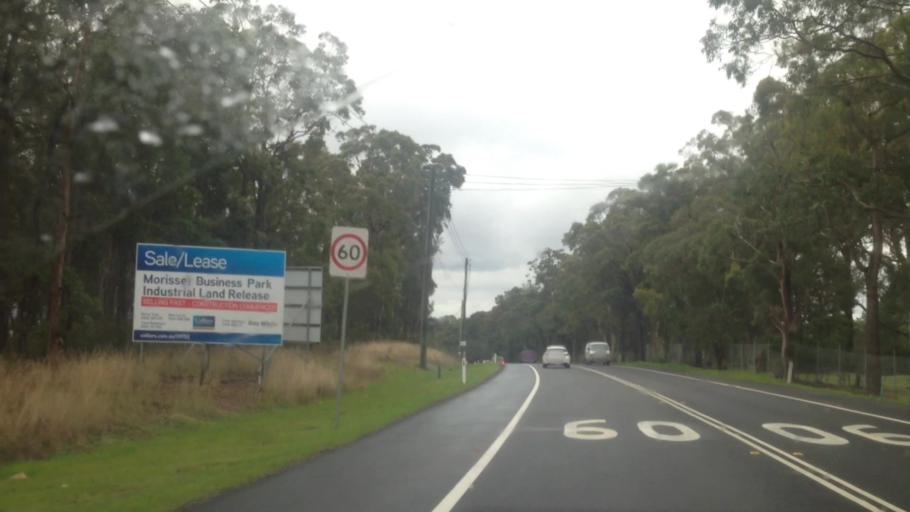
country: AU
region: New South Wales
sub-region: Lake Macquarie Shire
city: Dora Creek
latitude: -33.1191
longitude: 151.4779
